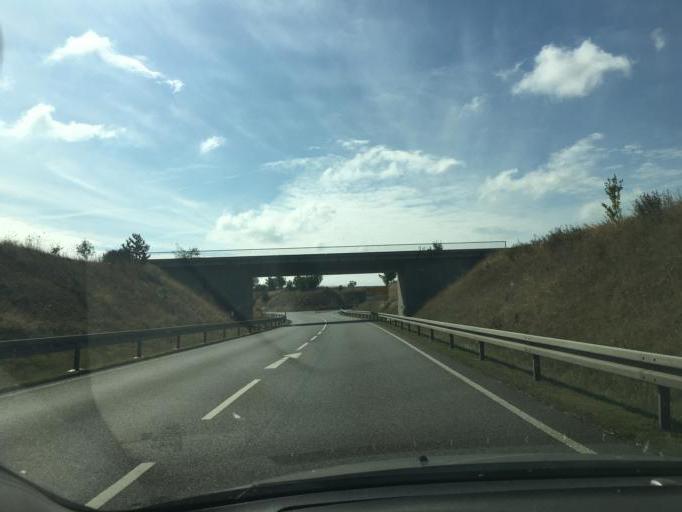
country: DE
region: Thuringia
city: Mittelpollnitz
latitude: 50.7507
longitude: 11.9068
